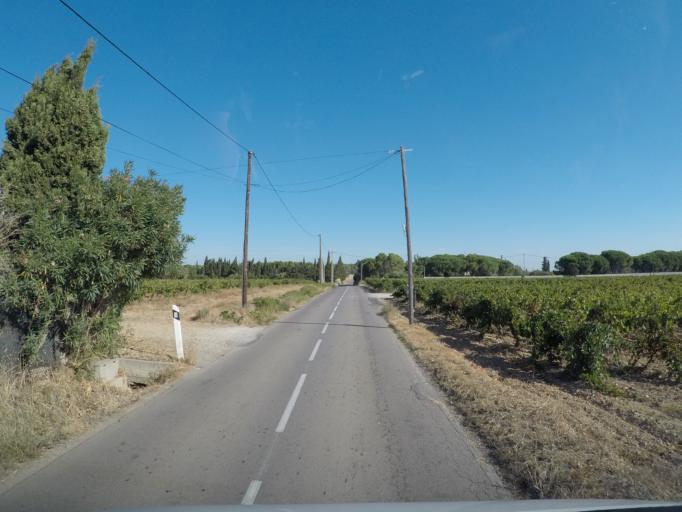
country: FR
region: Languedoc-Roussillon
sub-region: Departement de l'Aude
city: Narbonne
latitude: 43.1524
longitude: 3.0086
